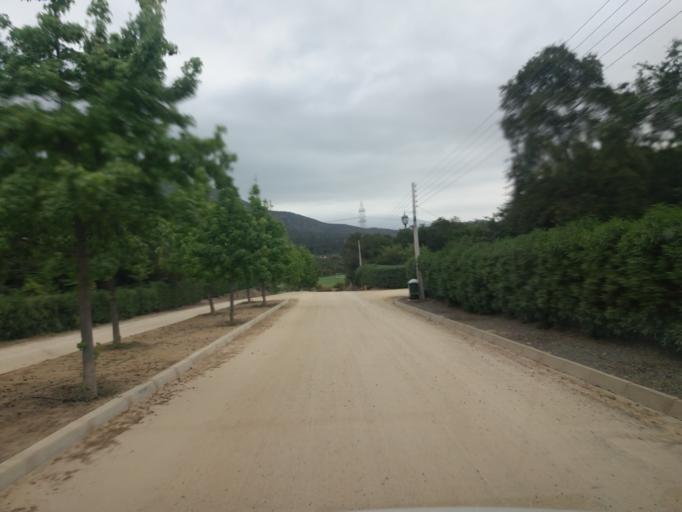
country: CL
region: Valparaiso
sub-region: Provincia de Marga Marga
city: Limache
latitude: -33.0278
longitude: -71.1355
